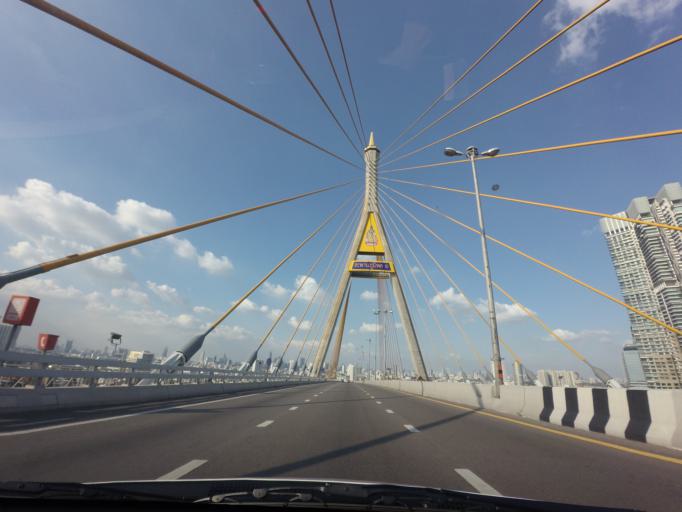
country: TH
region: Samut Prakan
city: Phra Pradaeng
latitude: 13.6697
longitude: 100.5385
